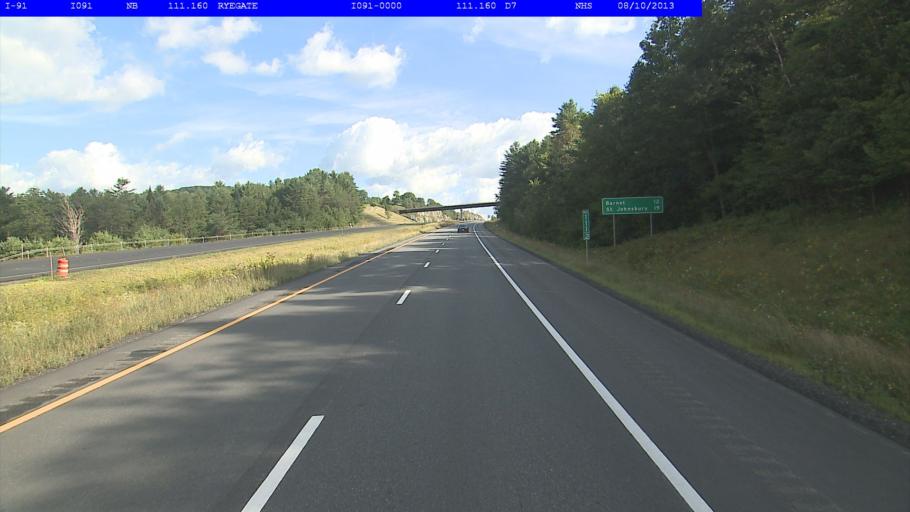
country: US
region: New Hampshire
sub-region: Grafton County
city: Woodsville
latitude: 44.1709
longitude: -72.0825
